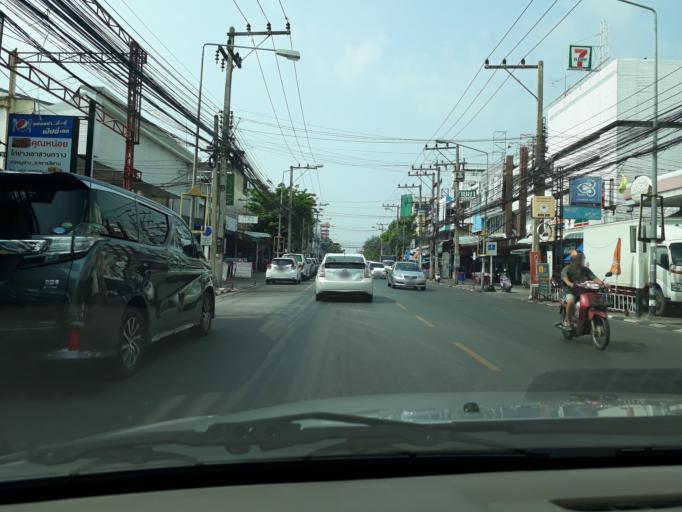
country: TH
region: Khon Kaen
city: Khon Kaen
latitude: 16.4316
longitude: 102.8358
